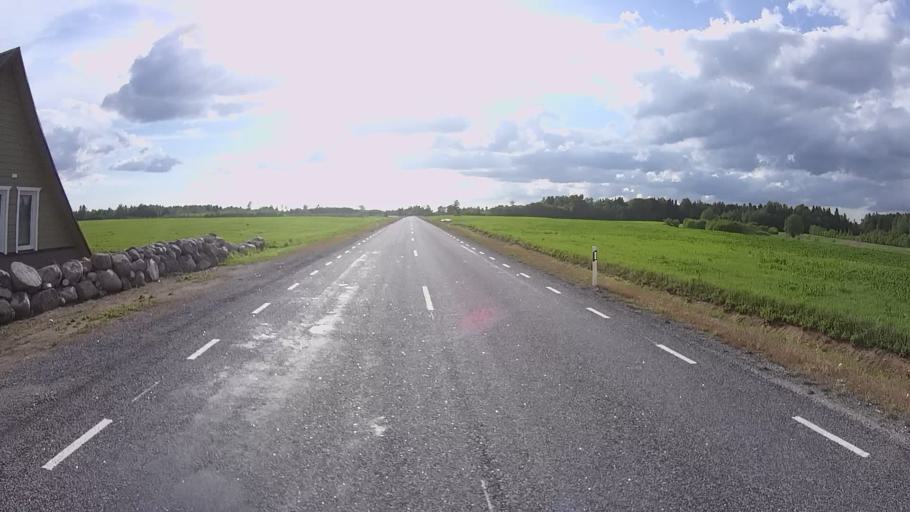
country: EE
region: Jogevamaa
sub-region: Mustvee linn
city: Mustvee
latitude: 59.0249
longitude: 27.0197
